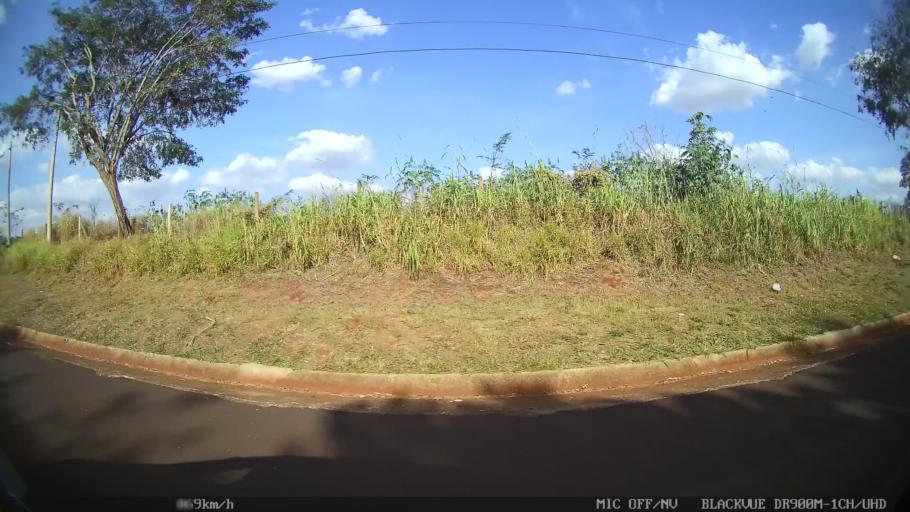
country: BR
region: Sao Paulo
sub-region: Ribeirao Preto
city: Ribeirao Preto
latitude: -21.1932
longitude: -47.8695
